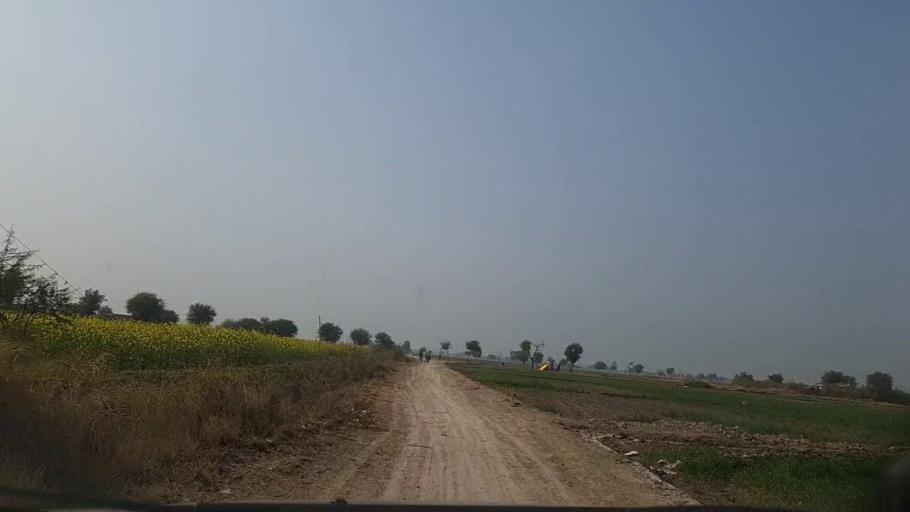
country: PK
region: Sindh
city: Sanghar
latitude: 26.0345
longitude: 68.9967
